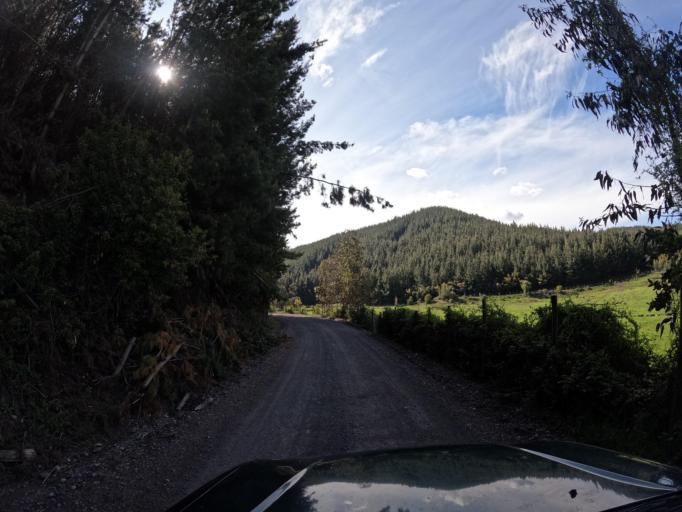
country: CL
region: Biobio
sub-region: Provincia de Concepcion
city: Chiguayante
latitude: -37.0638
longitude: -72.8986
